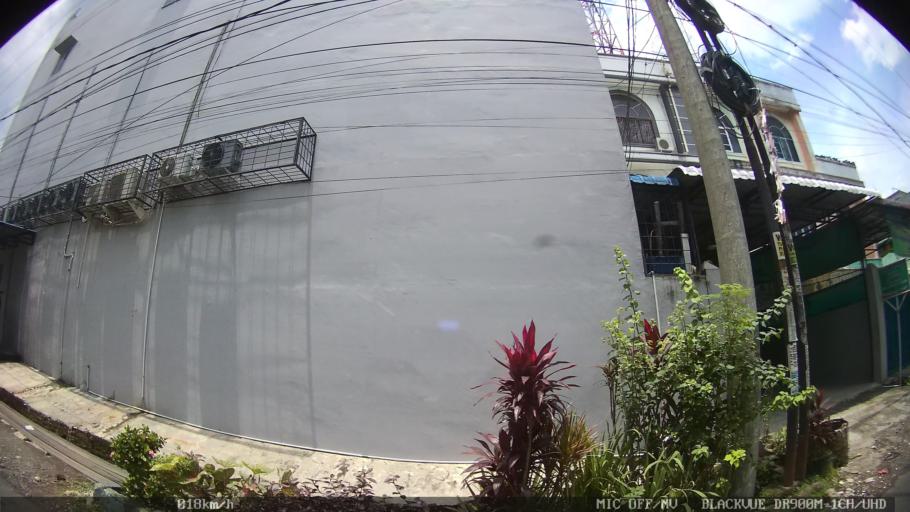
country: ID
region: North Sumatra
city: Medan
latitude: 3.6257
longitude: 98.6694
